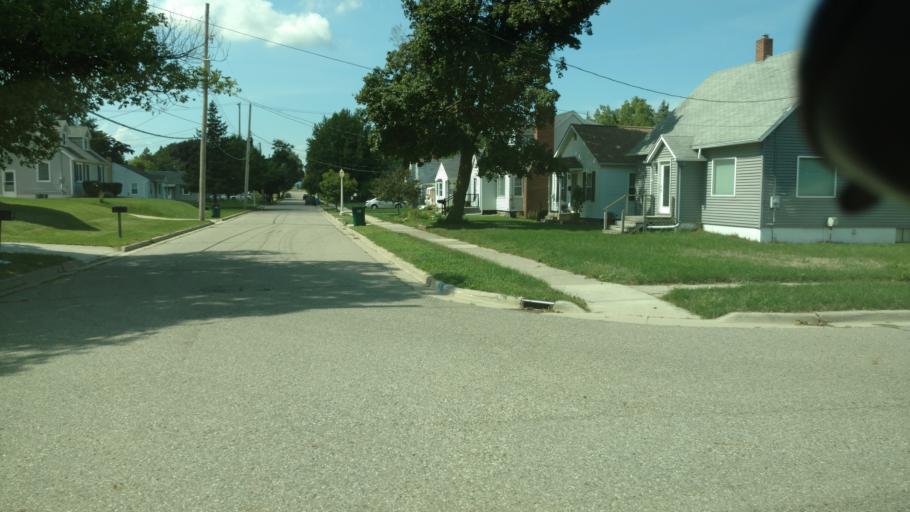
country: US
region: Michigan
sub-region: Ingham County
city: Lansing
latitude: 42.7567
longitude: -84.5482
